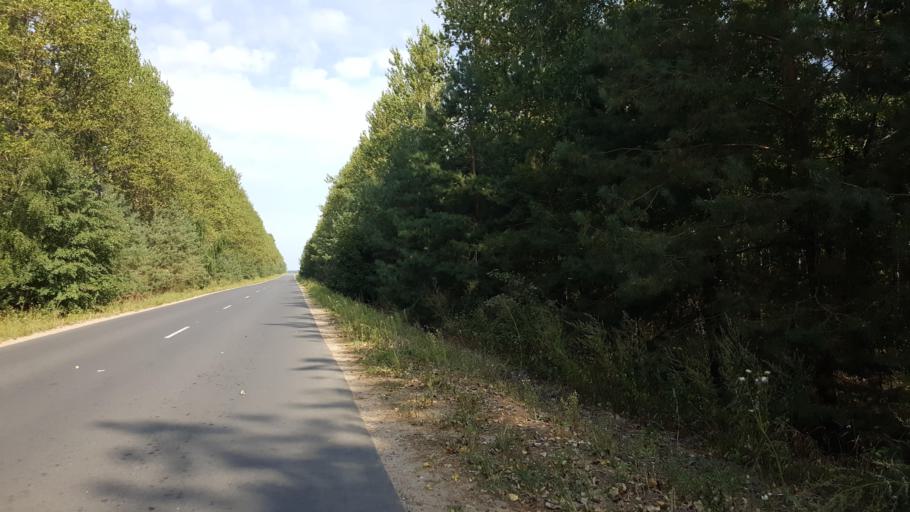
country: BY
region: Brest
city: Kamyanyets
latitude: 52.4496
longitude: 23.7374
